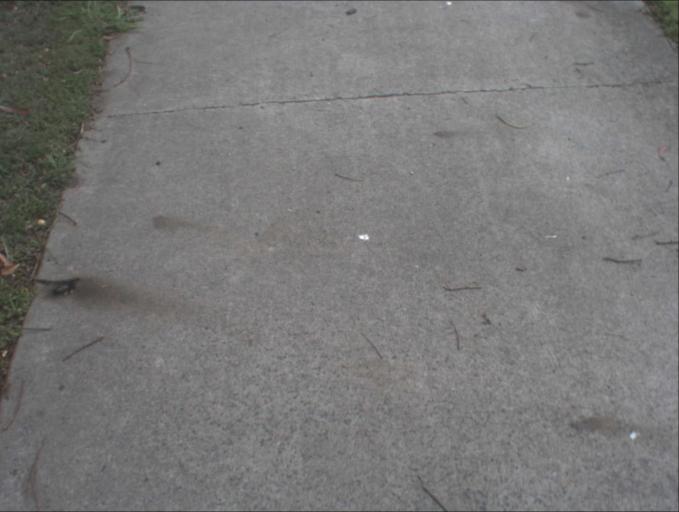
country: AU
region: Queensland
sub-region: Logan
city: Park Ridge South
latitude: -27.6932
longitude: 153.0349
